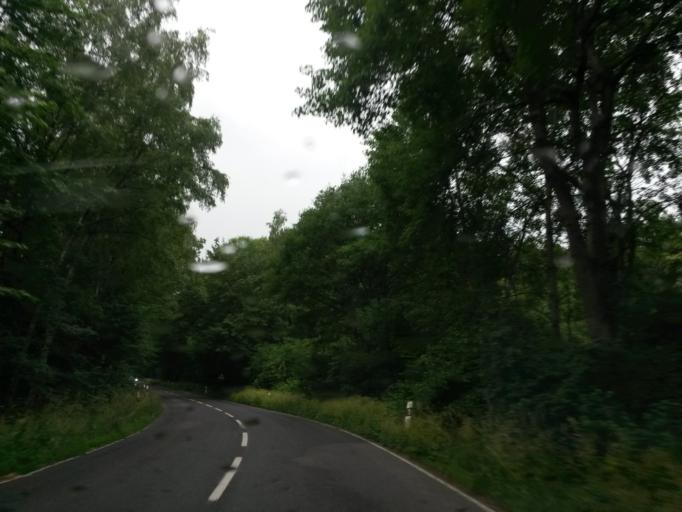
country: DE
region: North Rhine-Westphalia
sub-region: Regierungsbezirk Koln
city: Overath
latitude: 50.9124
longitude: 7.3244
